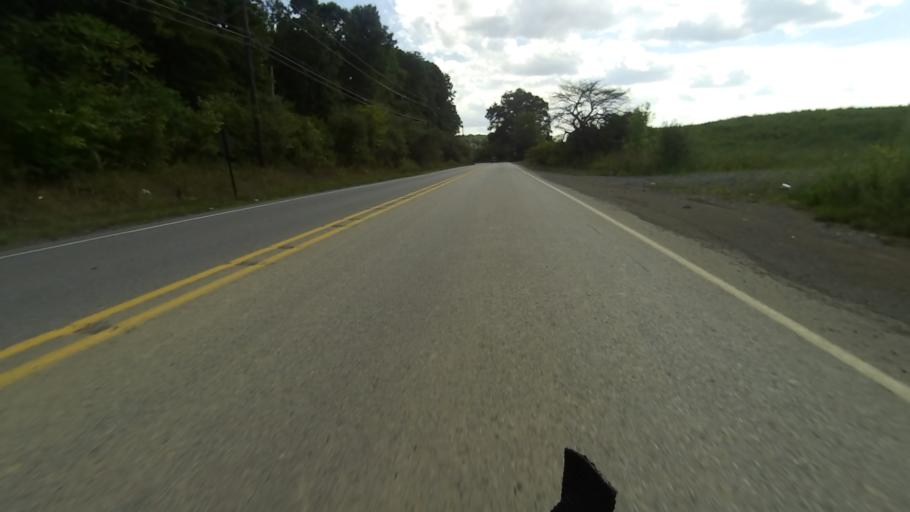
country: US
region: Pennsylvania
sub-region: Blair County
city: Greenwood
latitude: 40.5575
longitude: -78.3592
